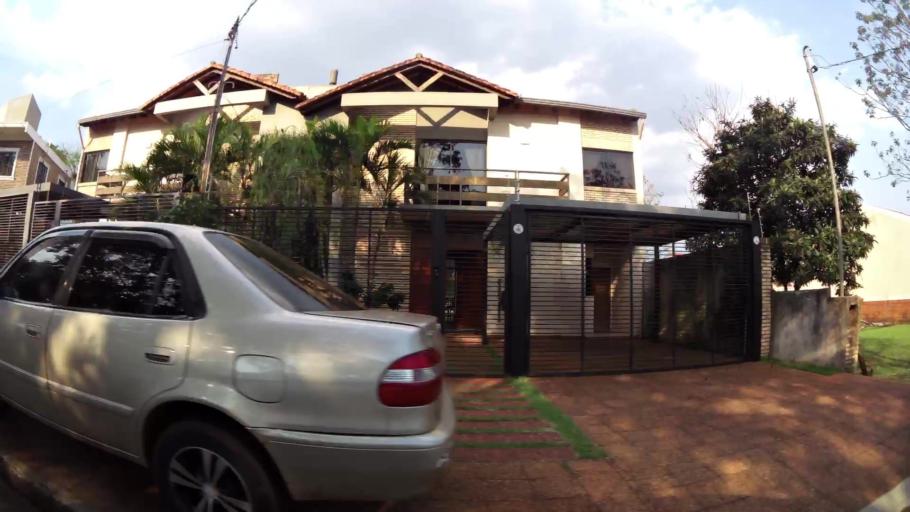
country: PY
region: Alto Parana
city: Presidente Franco
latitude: -25.5220
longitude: -54.6363
